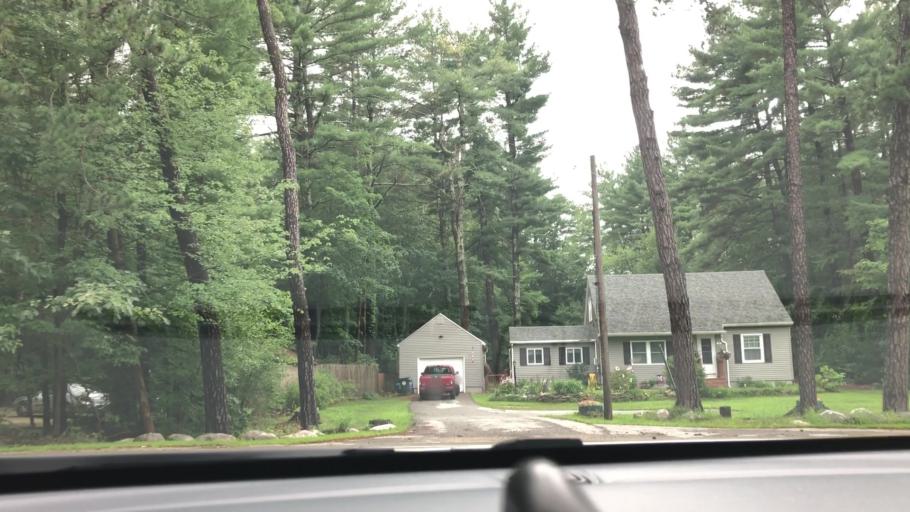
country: US
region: New Hampshire
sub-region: Hillsborough County
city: Pinardville
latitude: 43.0050
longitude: -71.5215
